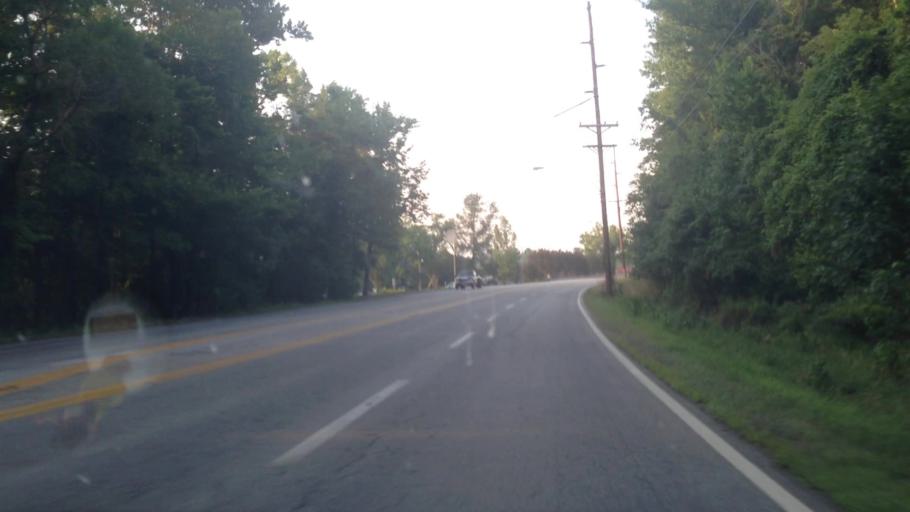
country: US
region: Virginia
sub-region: City of Danville
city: Danville
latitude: 36.5734
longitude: -79.4351
